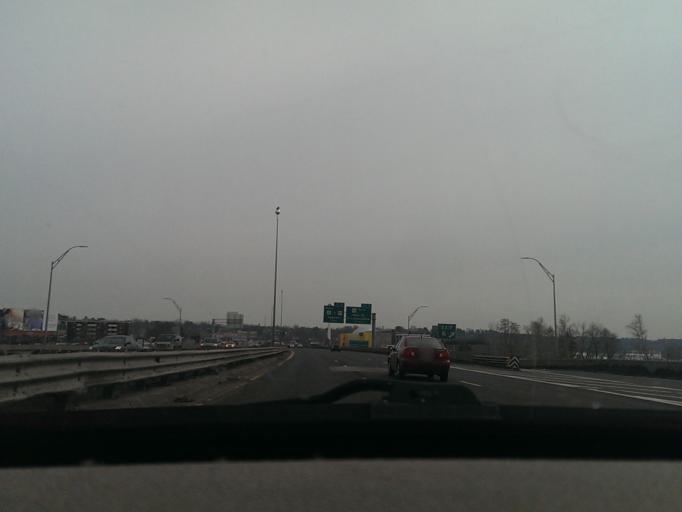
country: US
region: Massachusetts
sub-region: Hampden County
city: Springfield
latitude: 42.0990
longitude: -72.5899
